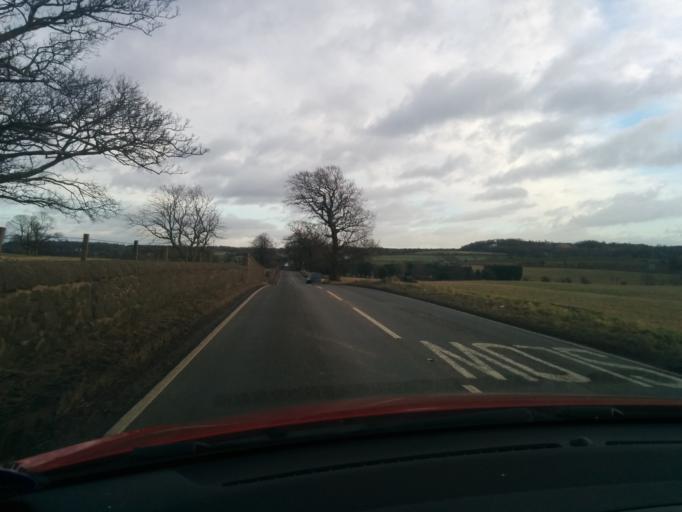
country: GB
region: Scotland
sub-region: Fife
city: Crossford
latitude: 55.9862
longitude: -3.5289
